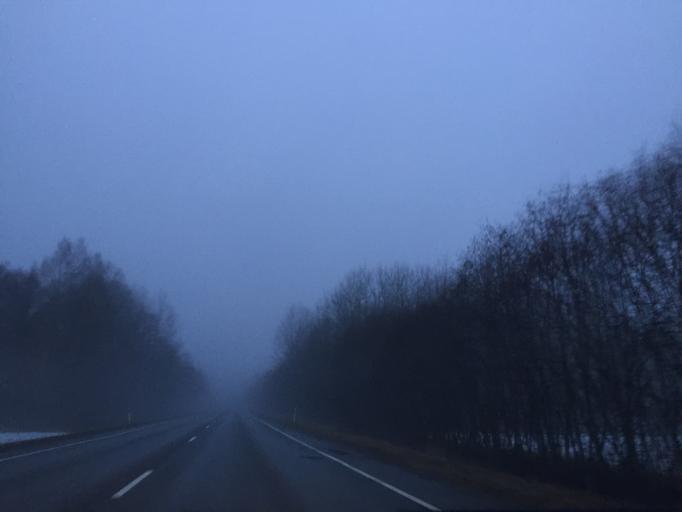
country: EE
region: Laeaene
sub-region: Lihula vald
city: Lihula
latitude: 58.6434
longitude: 23.6991
